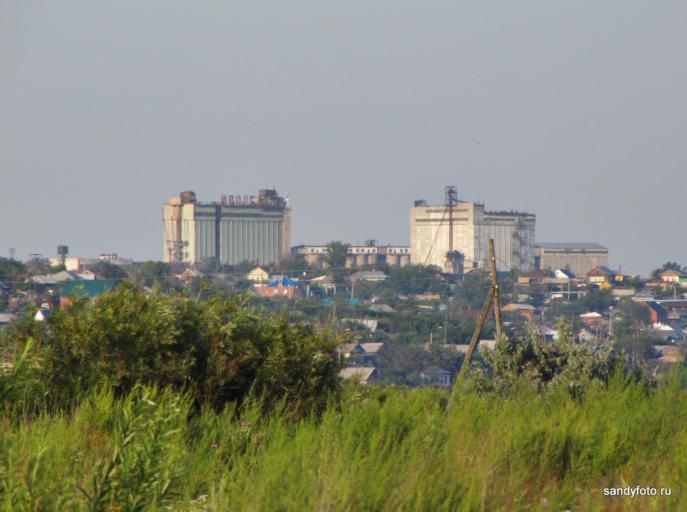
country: RU
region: Chelyabinsk
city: Troitsk
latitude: 54.0899
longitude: 61.5194
